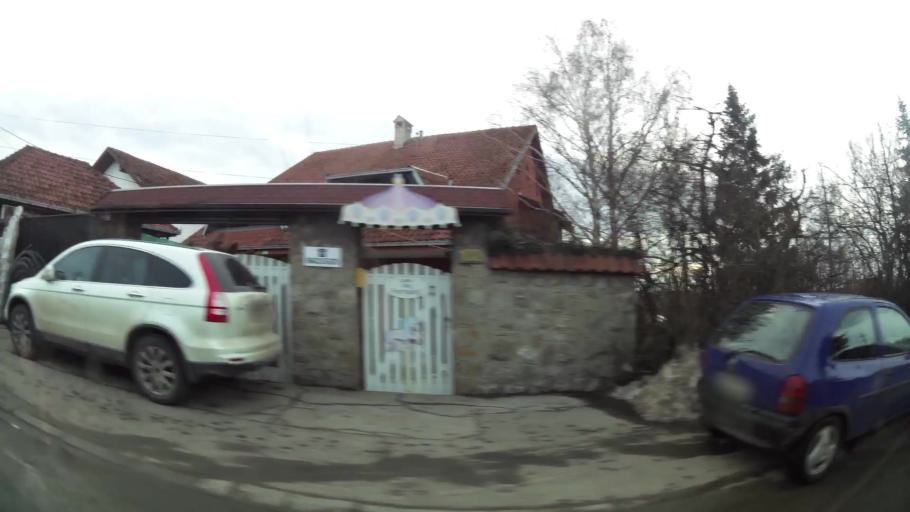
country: RS
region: Central Serbia
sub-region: Belgrade
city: Vozdovac
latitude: 44.7384
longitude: 20.4856
